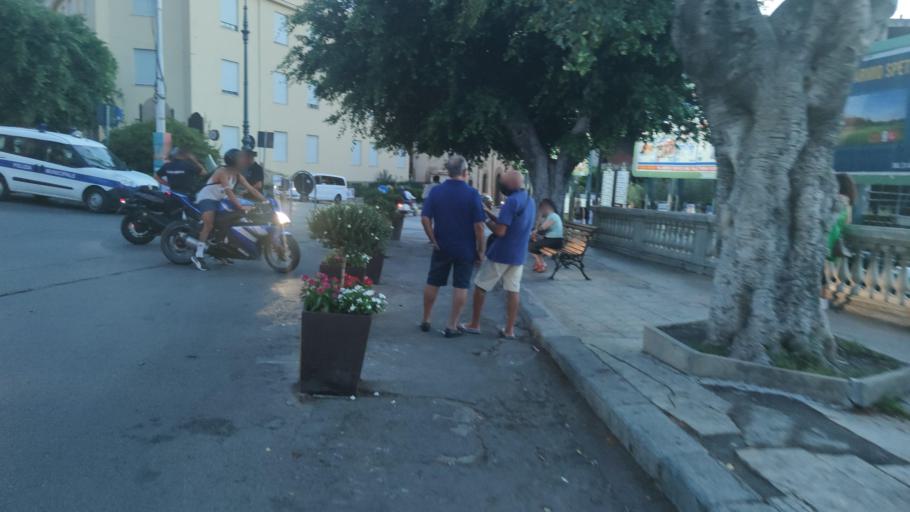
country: IT
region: Sicily
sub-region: Palermo
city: Cefalu
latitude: 38.0352
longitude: 14.0212
